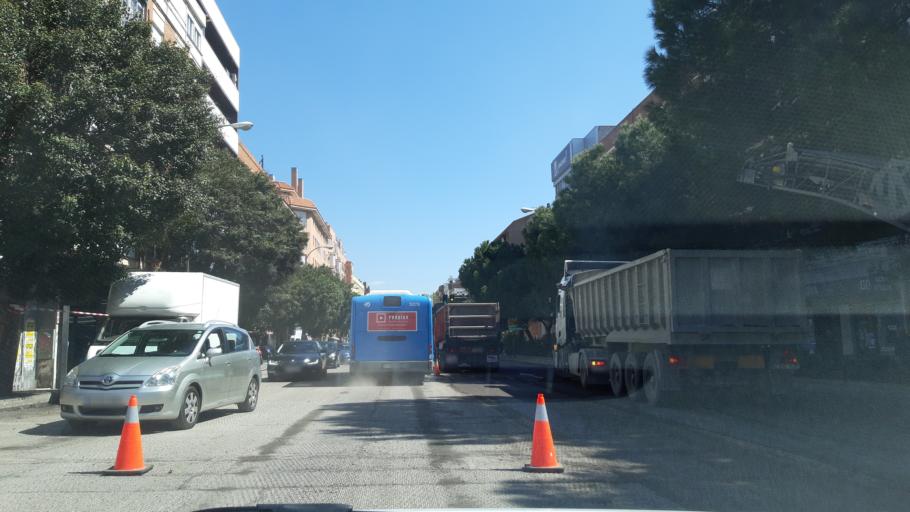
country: ES
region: Madrid
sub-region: Provincia de Madrid
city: San Blas
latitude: 40.4460
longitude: -3.6133
